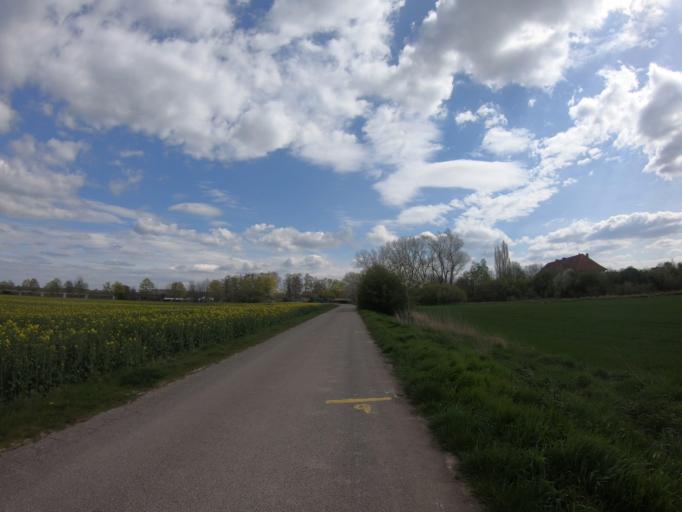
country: DE
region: Lower Saxony
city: Sarstedt
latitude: 52.2493
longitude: 9.8327
